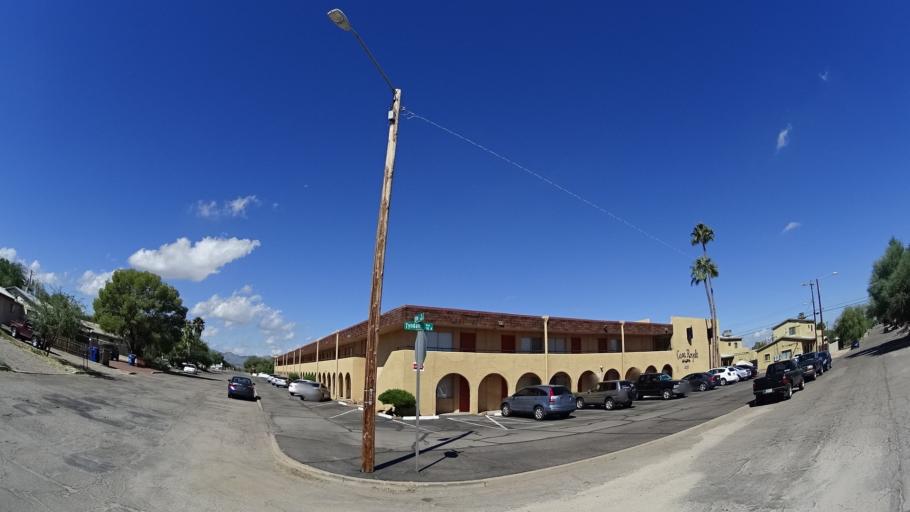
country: US
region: Arizona
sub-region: Pima County
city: Tucson
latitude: 32.2426
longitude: -110.9580
